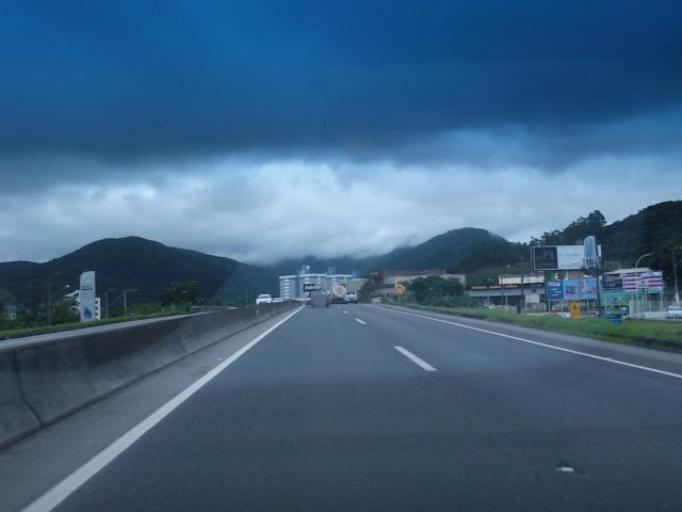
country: BR
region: Santa Catarina
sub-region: Itapema
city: Itapema
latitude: -27.0896
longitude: -48.6143
